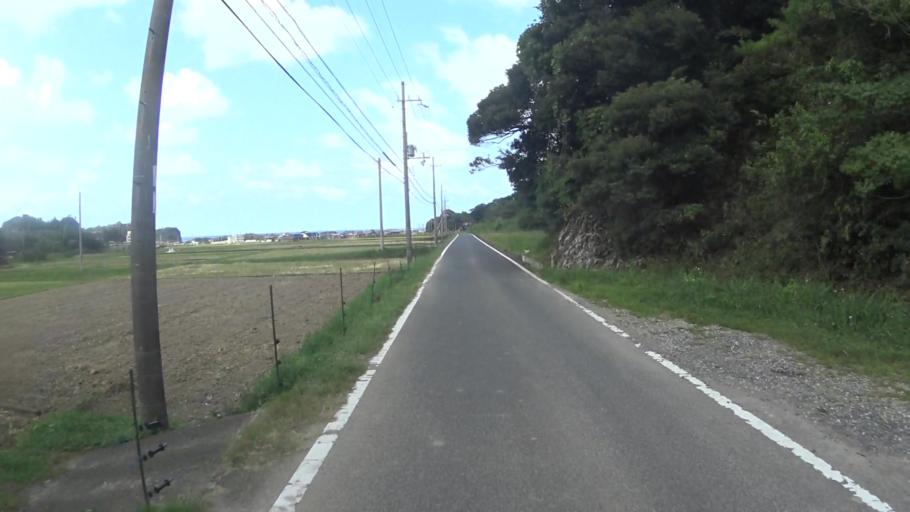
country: JP
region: Kyoto
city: Miyazu
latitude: 35.7509
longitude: 135.1768
